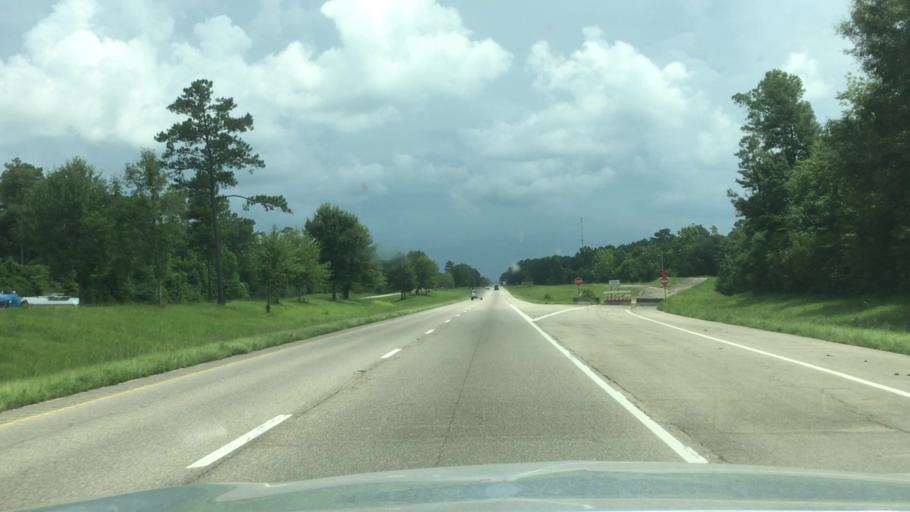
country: US
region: Mississippi
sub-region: Pearl River County
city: Picayune
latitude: 30.5608
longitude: -89.6398
